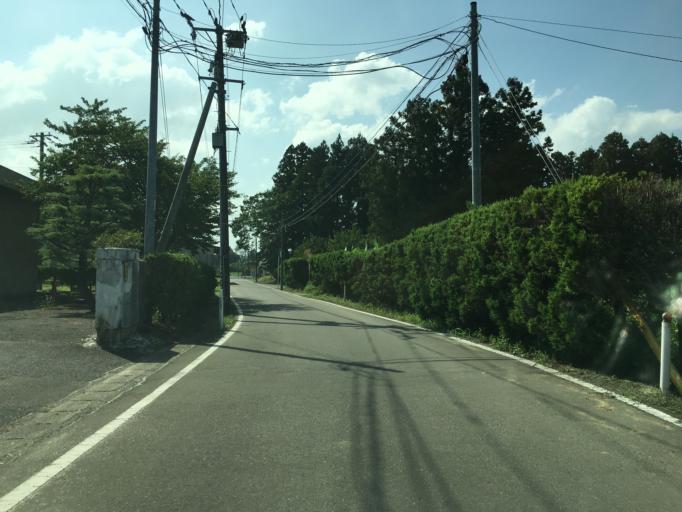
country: JP
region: Miyagi
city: Kakuda
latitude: 37.9434
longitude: 140.8051
